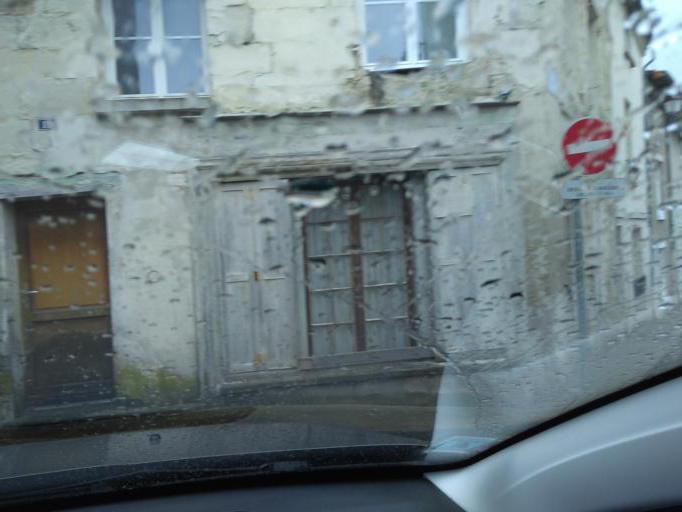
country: FR
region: Poitou-Charentes
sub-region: Departement de la Vienne
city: Loudun
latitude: 47.0082
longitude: 0.0852
